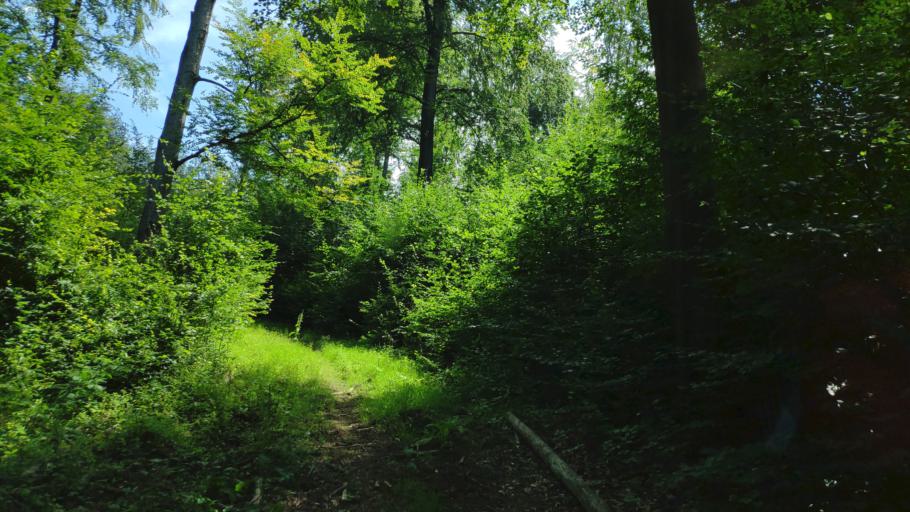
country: SK
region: Kosicky
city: Dobsina
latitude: 48.7115
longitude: 20.3870
